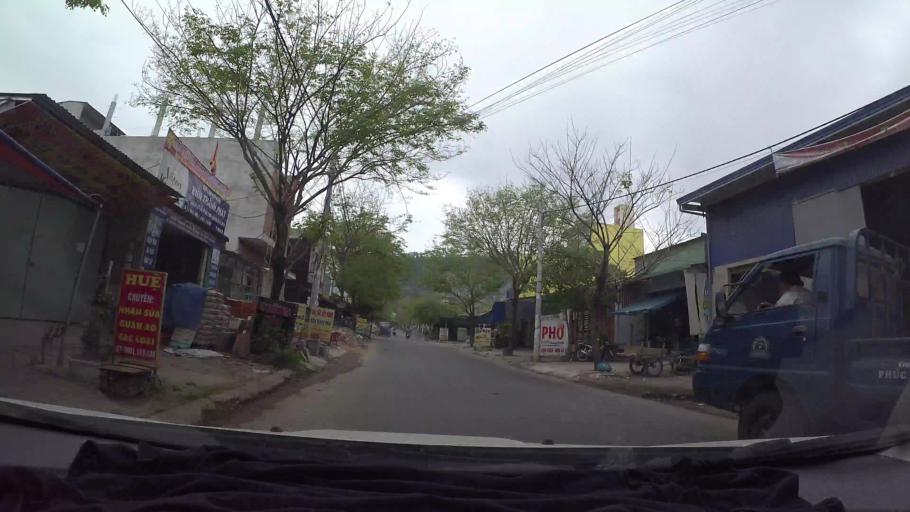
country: VN
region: Da Nang
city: Lien Chieu
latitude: 16.0426
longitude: 108.1724
